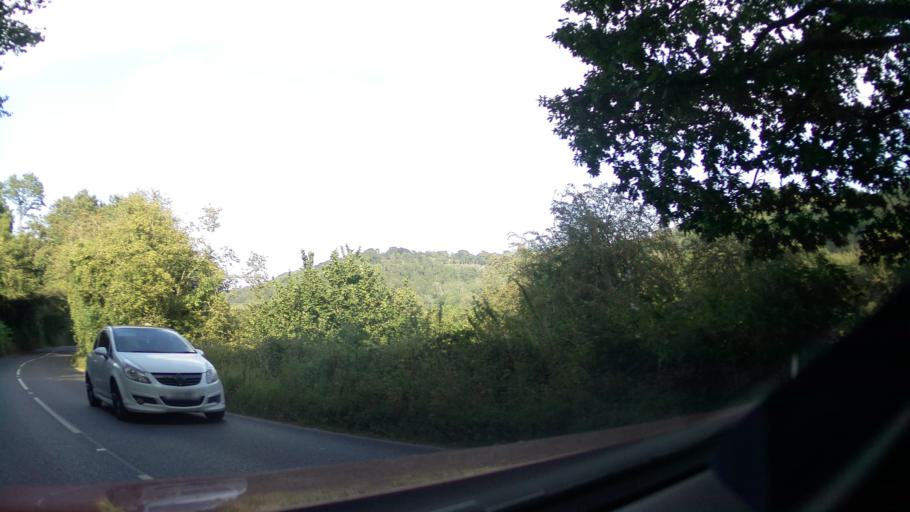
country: GB
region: England
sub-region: Devon
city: Tiverton
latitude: 50.8643
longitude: -3.5048
